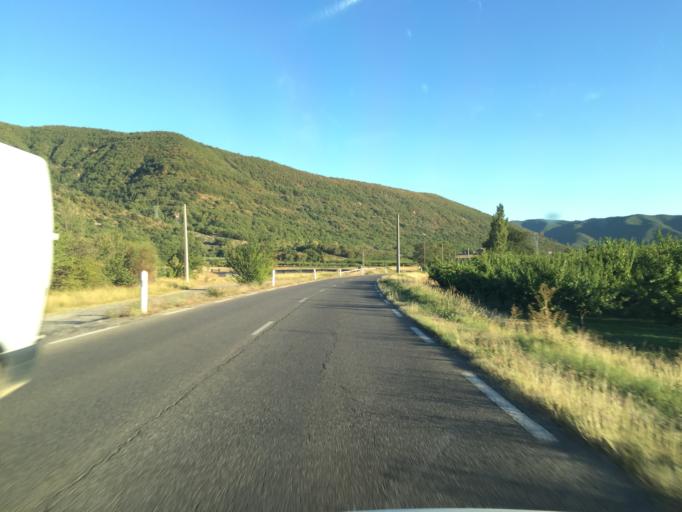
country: FR
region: Provence-Alpes-Cote d'Azur
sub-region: Departement des Alpes-de-Haute-Provence
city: Malijai
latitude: 44.0738
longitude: 6.0217
